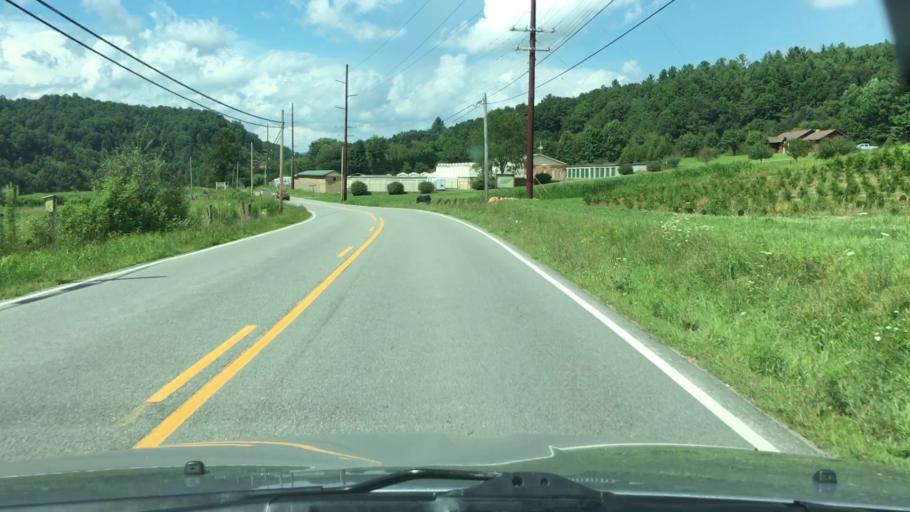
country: US
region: North Carolina
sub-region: Yancey County
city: Burnsville
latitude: 35.8885
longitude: -82.2148
